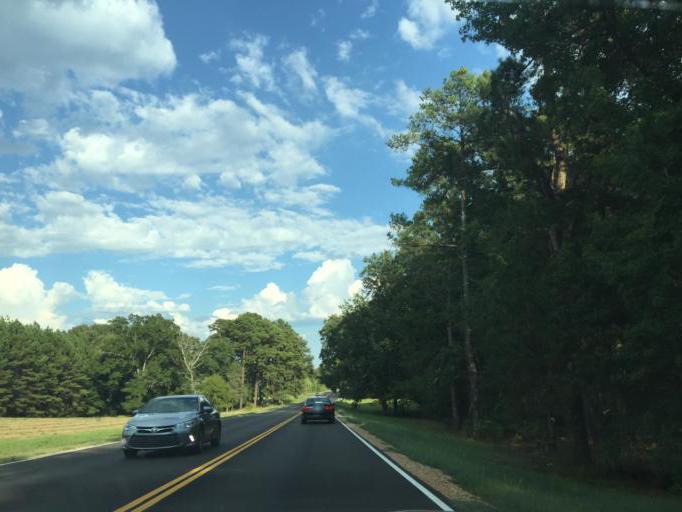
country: US
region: Mississippi
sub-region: Madison County
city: Ridgeland
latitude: 32.4274
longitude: -90.1138
